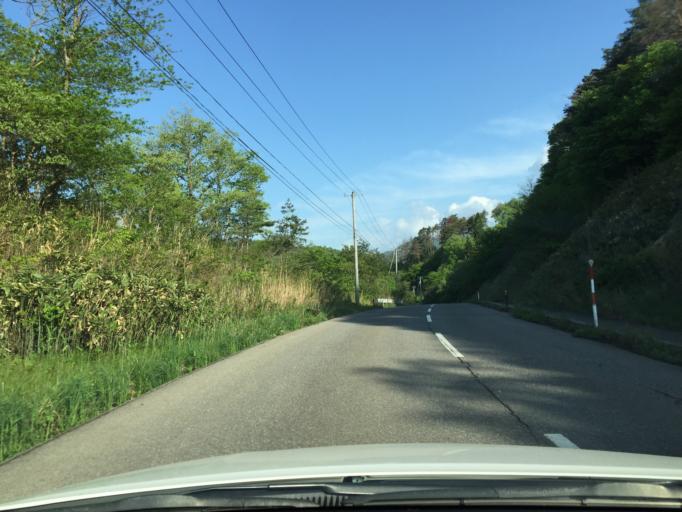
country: JP
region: Fukushima
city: Kitakata
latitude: 37.6522
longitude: 139.7646
